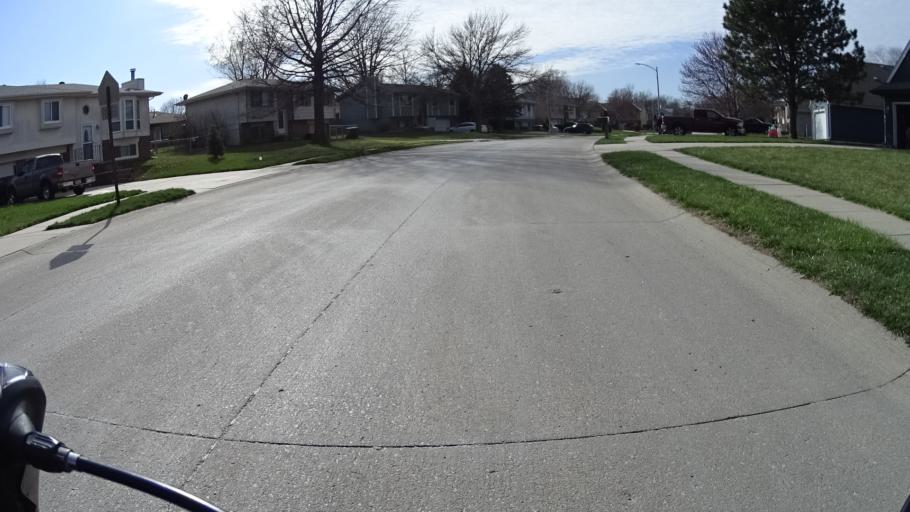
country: US
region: Nebraska
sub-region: Sarpy County
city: Offutt Air Force Base
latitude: 41.1123
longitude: -95.9576
